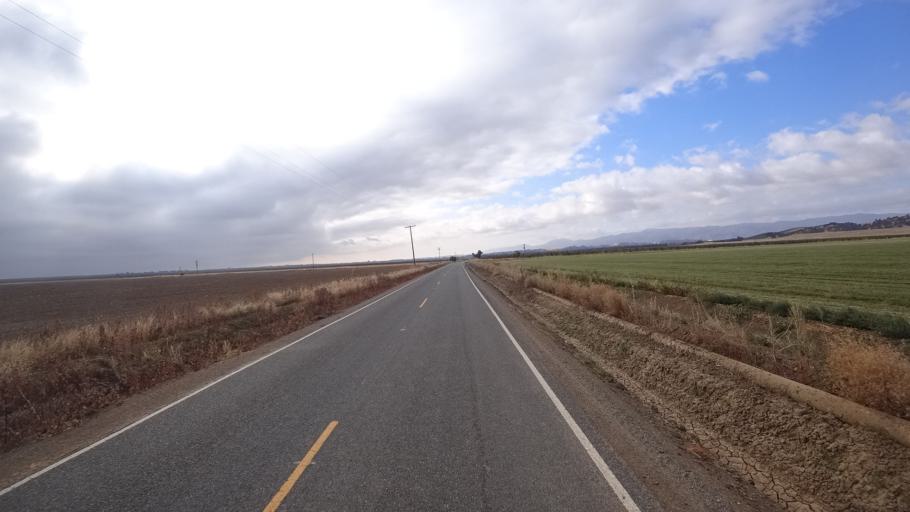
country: US
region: California
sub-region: Yolo County
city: Esparto
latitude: 38.7395
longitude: -122.0449
